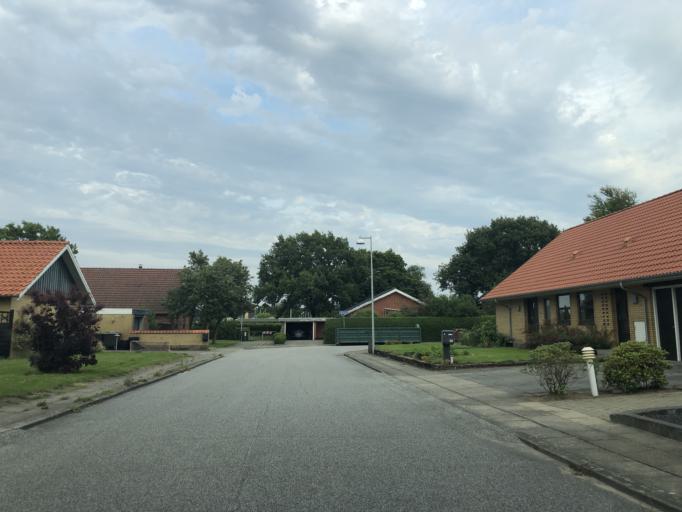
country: DK
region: Central Jutland
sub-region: Herning Kommune
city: Herning
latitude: 56.1483
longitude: 8.9533
